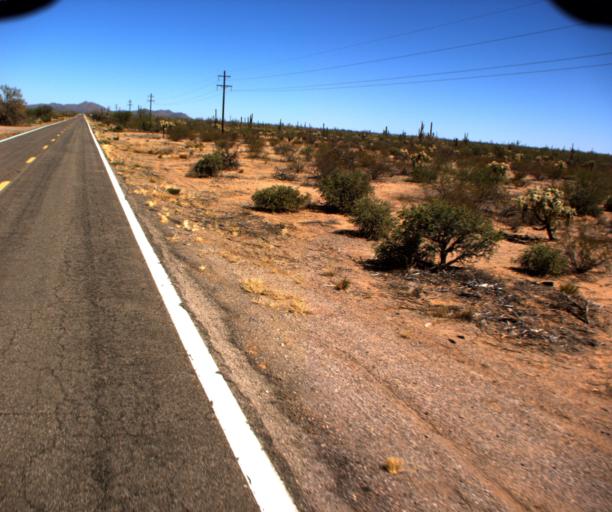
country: US
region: Arizona
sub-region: Pima County
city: Sells
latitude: 32.0990
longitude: -112.0646
